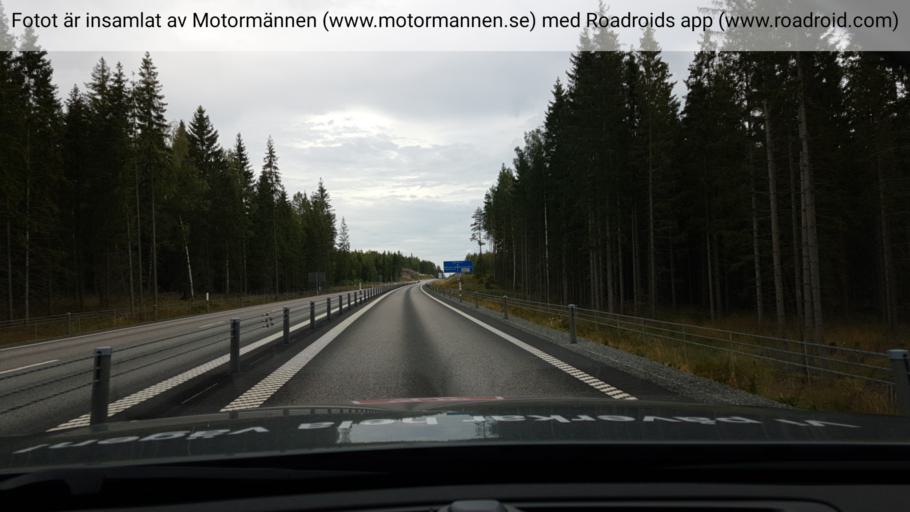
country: SE
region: Uppsala
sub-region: Heby Kommun
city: Heby
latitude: 60.0114
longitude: 16.8524
